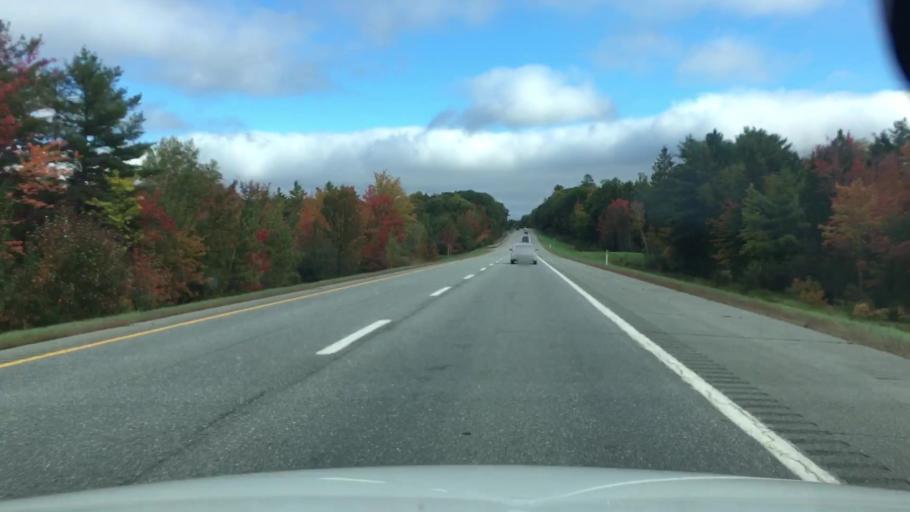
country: US
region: Maine
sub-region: Penobscot County
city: Carmel
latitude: 44.7642
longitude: -68.9905
